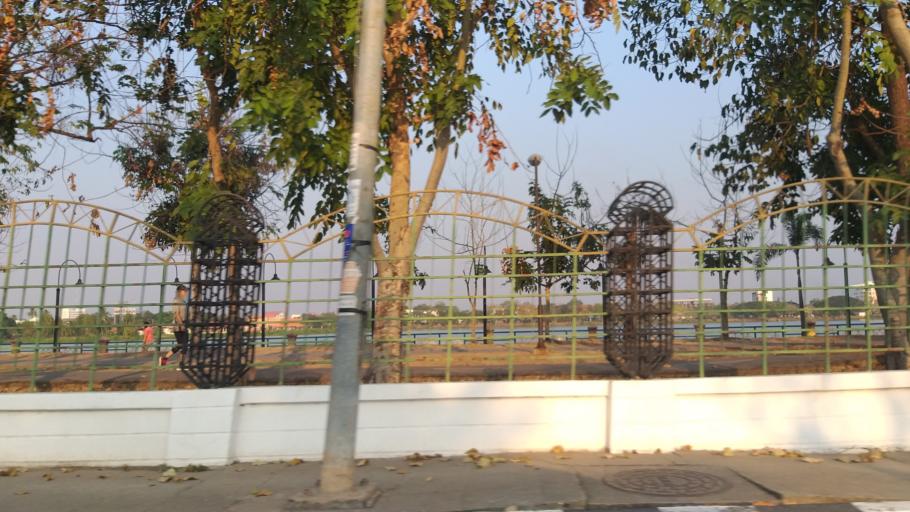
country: TH
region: Khon Kaen
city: Khon Kaen
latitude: 16.4155
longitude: 102.8352
